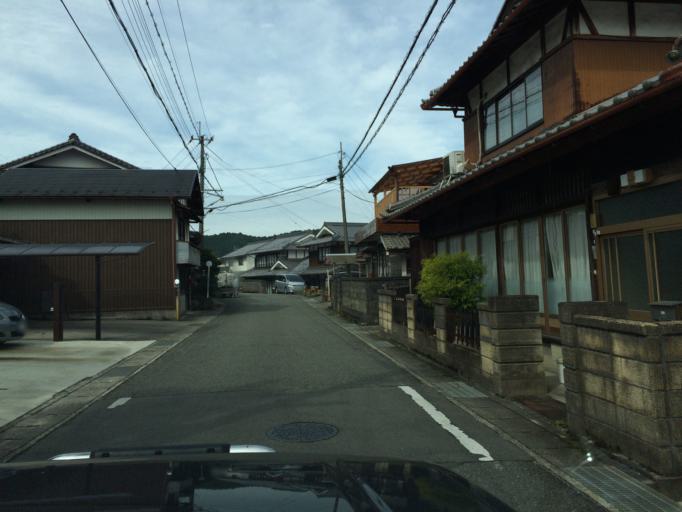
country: JP
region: Hyogo
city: Sasayama
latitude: 35.0715
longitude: 135.3387
